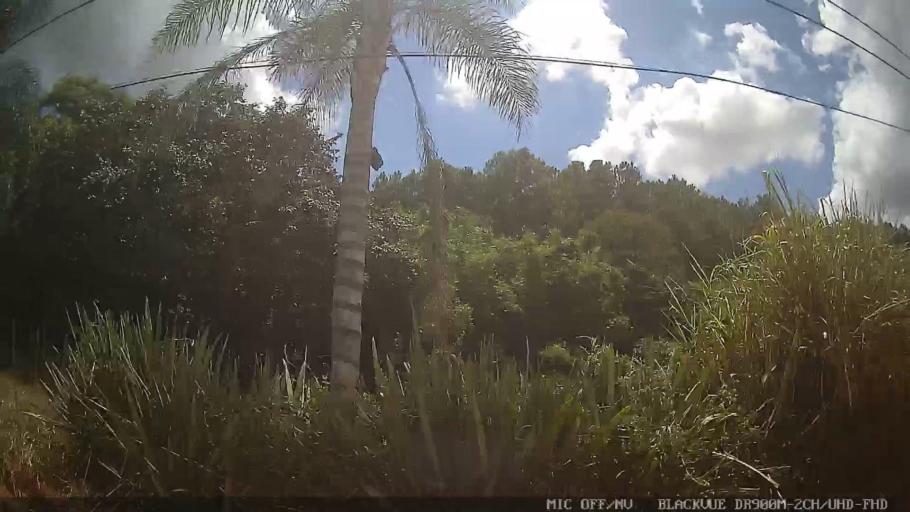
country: BR
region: Sao Paulo
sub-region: Jarinu
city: Jarinu
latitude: -23.1379
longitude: -46.6426
